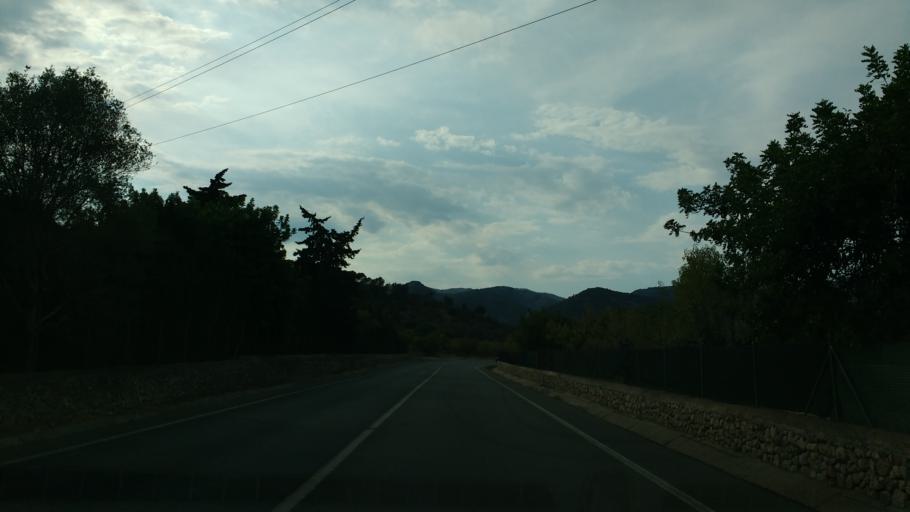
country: ES
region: Balearic Islands
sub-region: Illes Balears
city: Alaro
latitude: 39.6902
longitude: 2.8053
